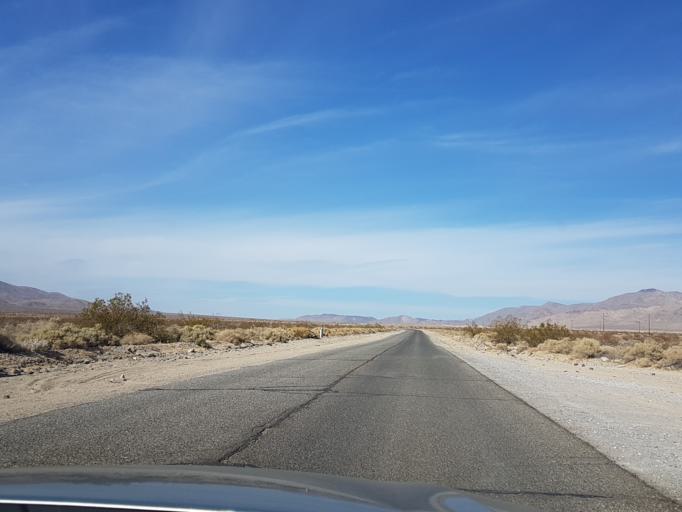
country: US
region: California
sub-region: San Bernardino County
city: Searles Valley
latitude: 35.8294
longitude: -117.3386
